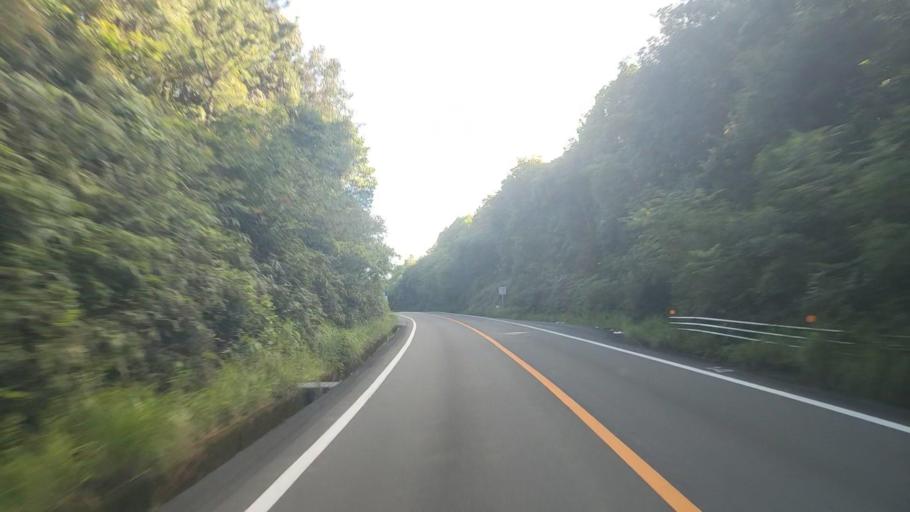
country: JP
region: Mie
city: Toba
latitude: 34.3472
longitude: 136.8402
